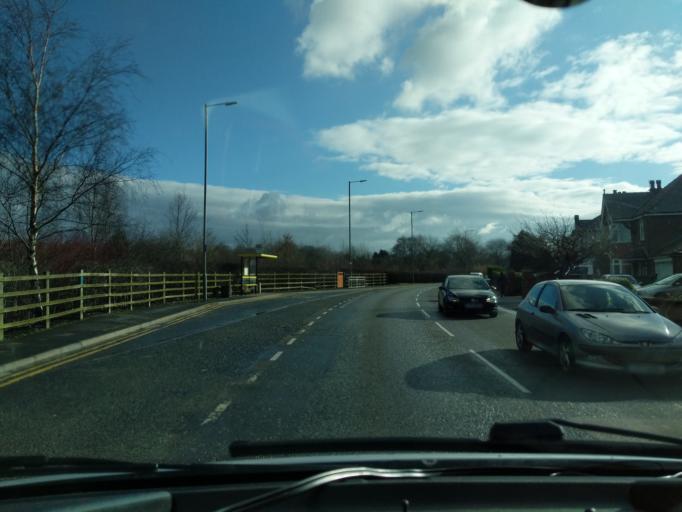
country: GB
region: England
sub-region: St. Helens
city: Eccleston
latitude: 53.4684
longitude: -2.7660
